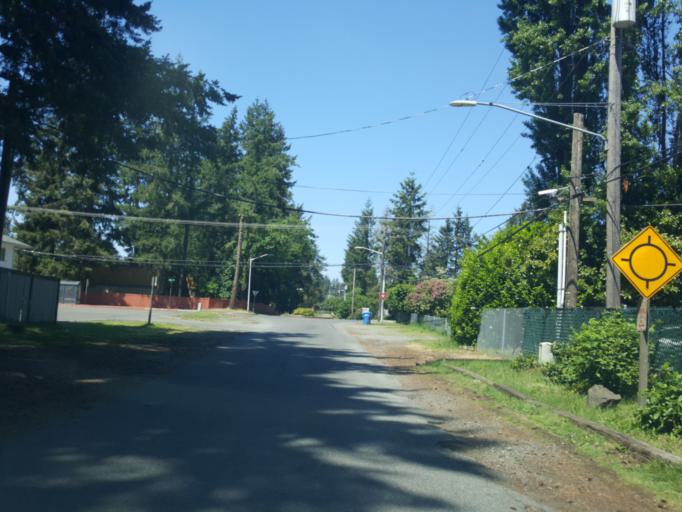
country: US
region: Washington
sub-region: Pierce County
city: McChord Air Force Base
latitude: 47.1411
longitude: -122.5075
